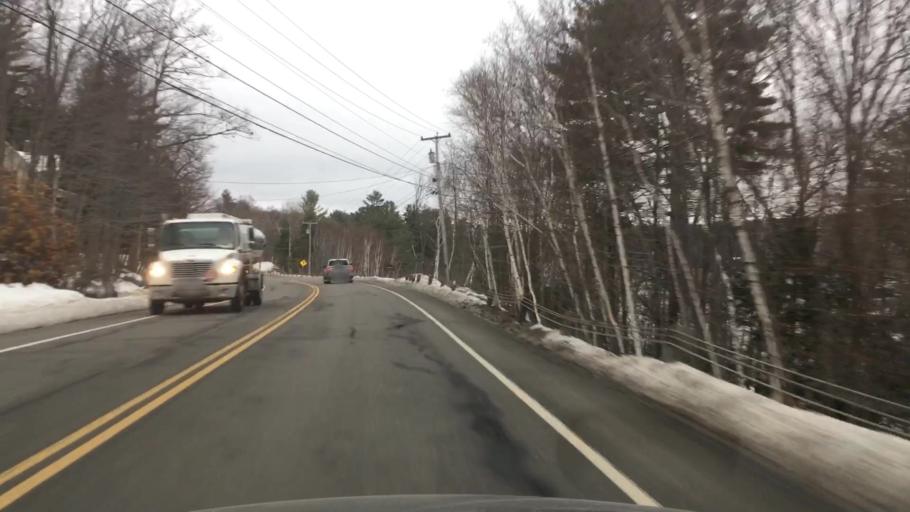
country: US
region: New Hampshire
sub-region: Merrimack County
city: Newbury
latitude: 43.3273
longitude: -72.0430
